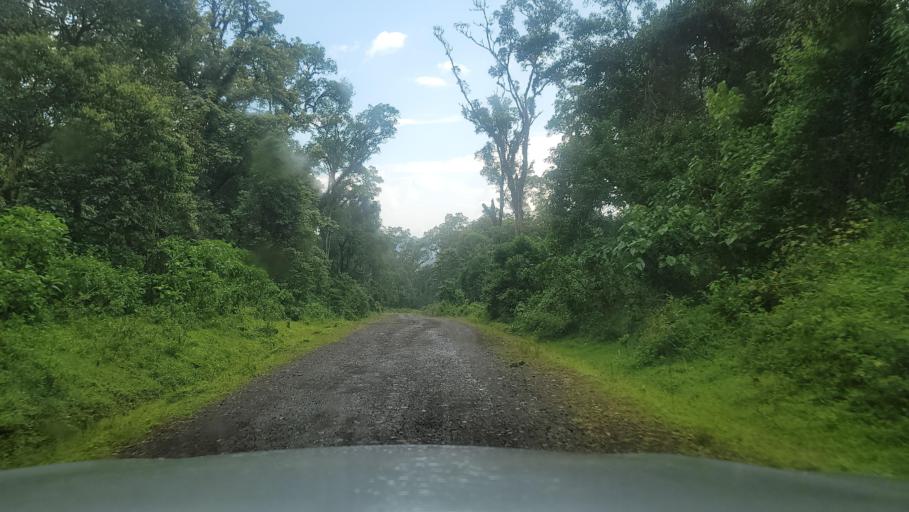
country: ET
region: Southern Nations, Nationalities, and People's Region
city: Bonga
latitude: 7.6510
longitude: 36.2467
